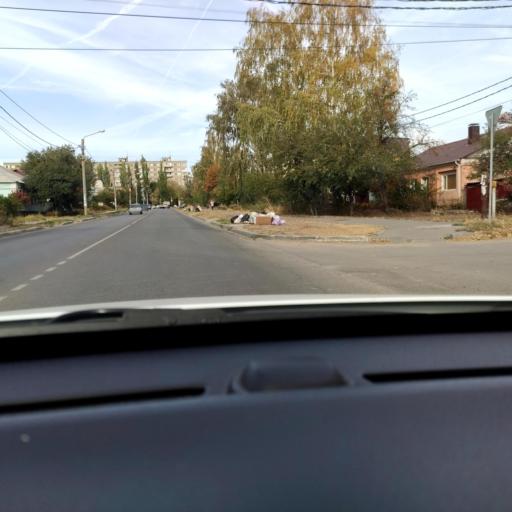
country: RU
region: Voronezj
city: Podgornoye
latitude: 51.6992
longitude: 39.1567
